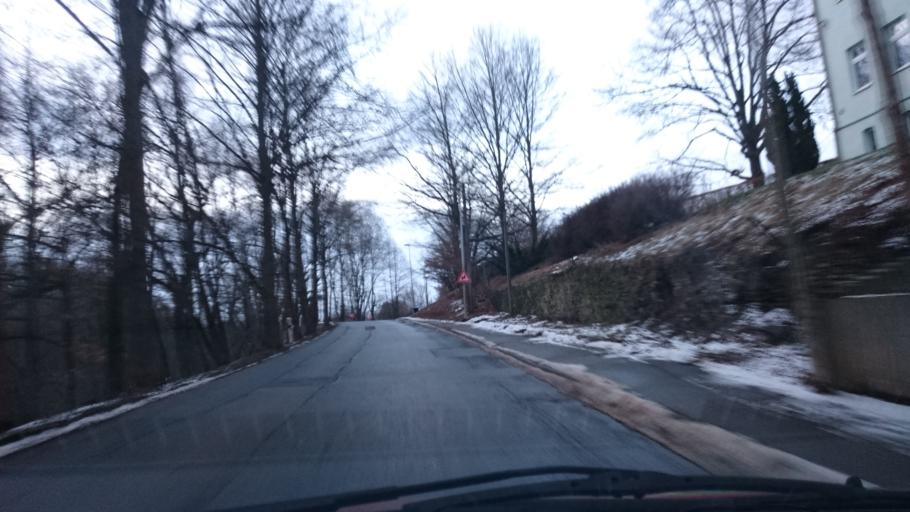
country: DE
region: Saxony
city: Wilkau-Hasslau
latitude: 50.7044
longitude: 12.5157
